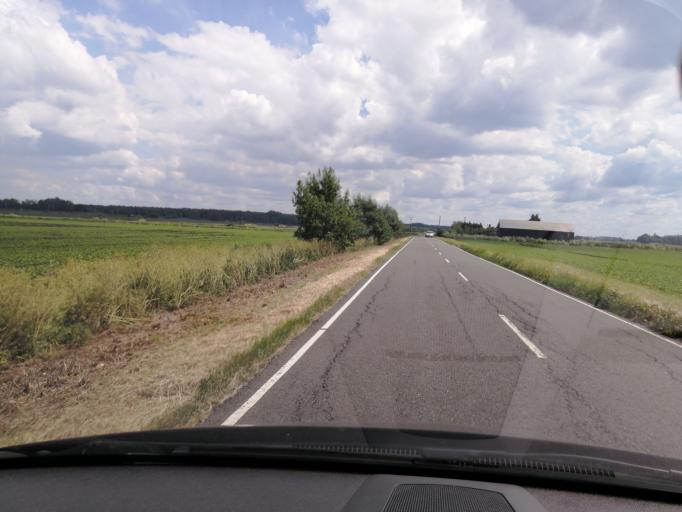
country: GB
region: England
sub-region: Cambridgeshire
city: Yaxley
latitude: 52.4999
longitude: -0.2496
